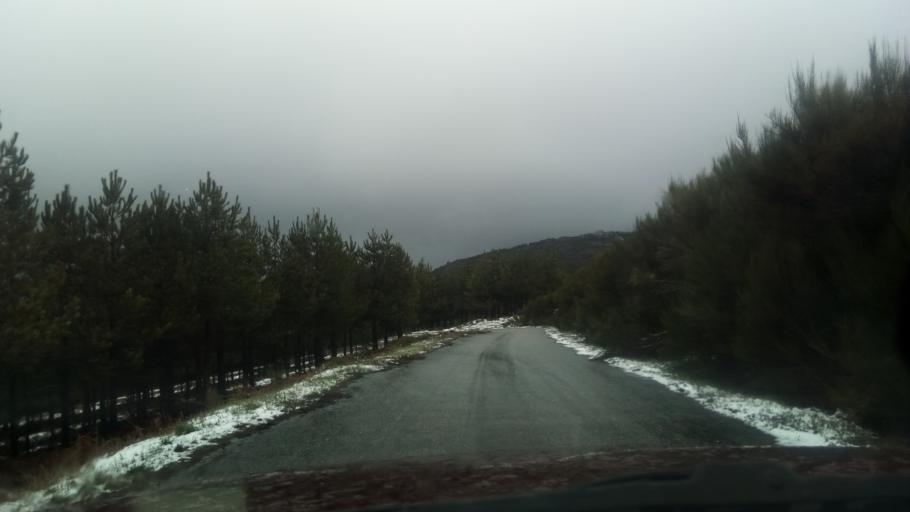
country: PT
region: Guarda
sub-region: Celorico da Beira
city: Celorico da Beira
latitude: 40.5171
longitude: -7.4544
